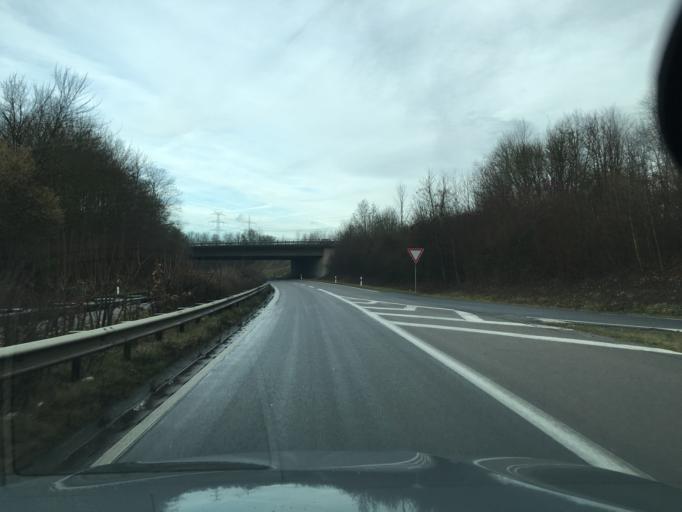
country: DE
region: Rheinland-Pfalz
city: Bad Neuenahr-Ahrweiler
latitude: 50.5743
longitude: 7.1177
